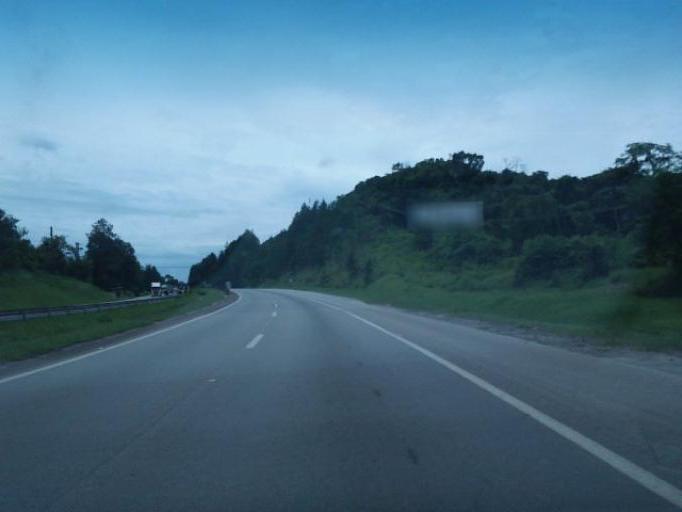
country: BR
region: Sao Paulo
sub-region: Juquitiba
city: Juquitiba
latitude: -23.9439
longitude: -47.0967
